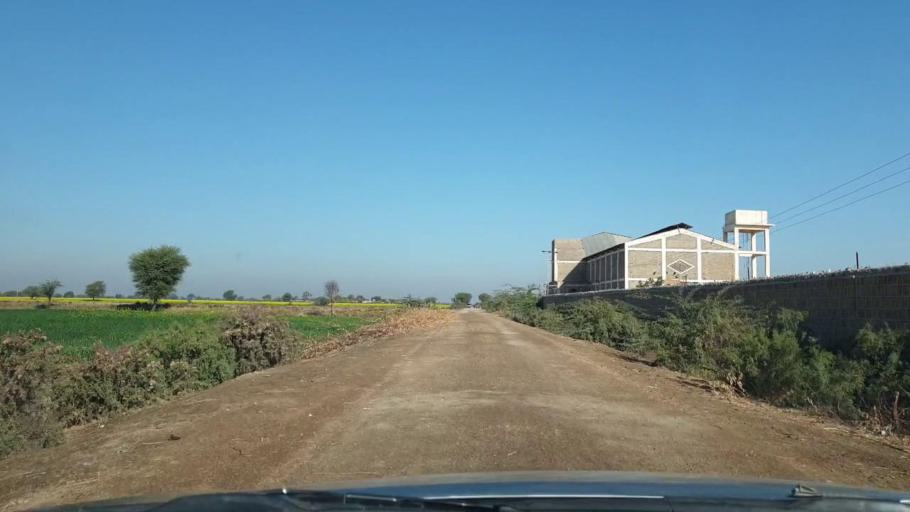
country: PK
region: Sindh
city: Jhol
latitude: 25.8144
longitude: 68.9652
